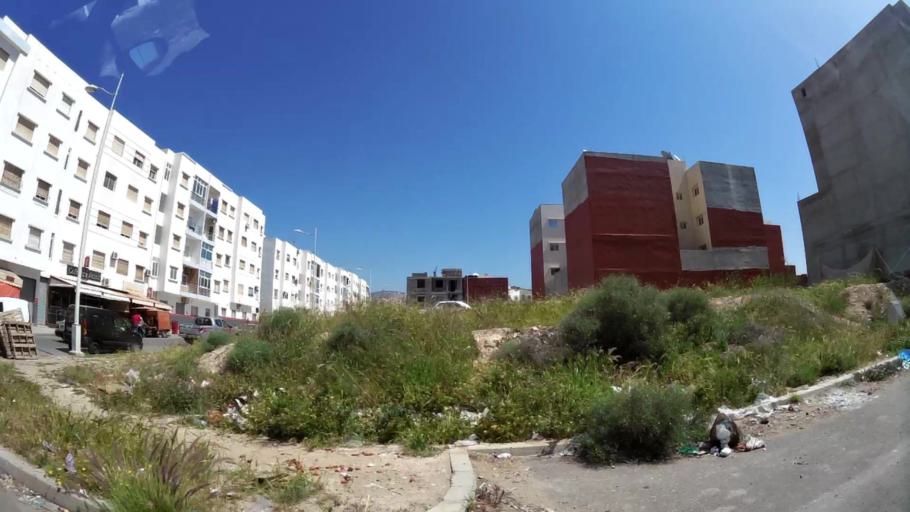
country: MA
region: Oued ed Dahab-Lagouira
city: Dakhla
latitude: 30.4402
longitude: -9.5594
